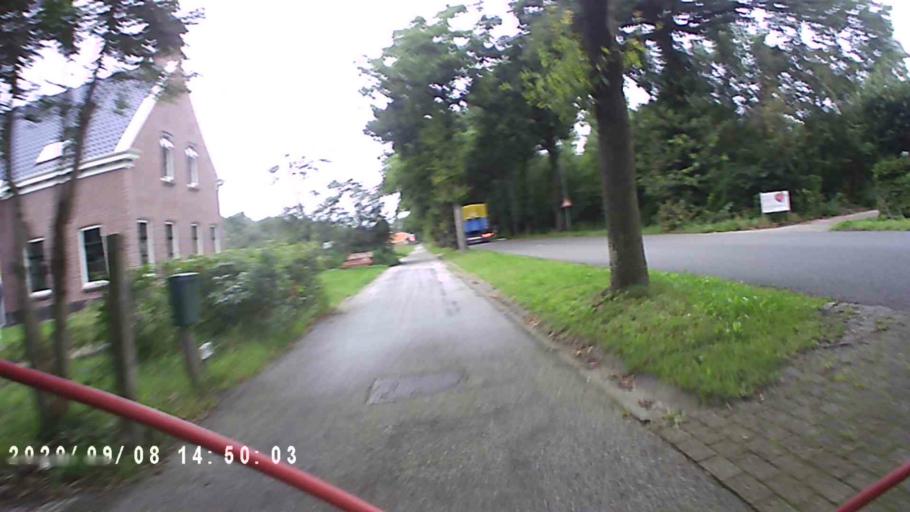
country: NL
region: Groningen
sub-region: Gemeente Slochteren
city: Slochteren
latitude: 53.2436
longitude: 6.8010
